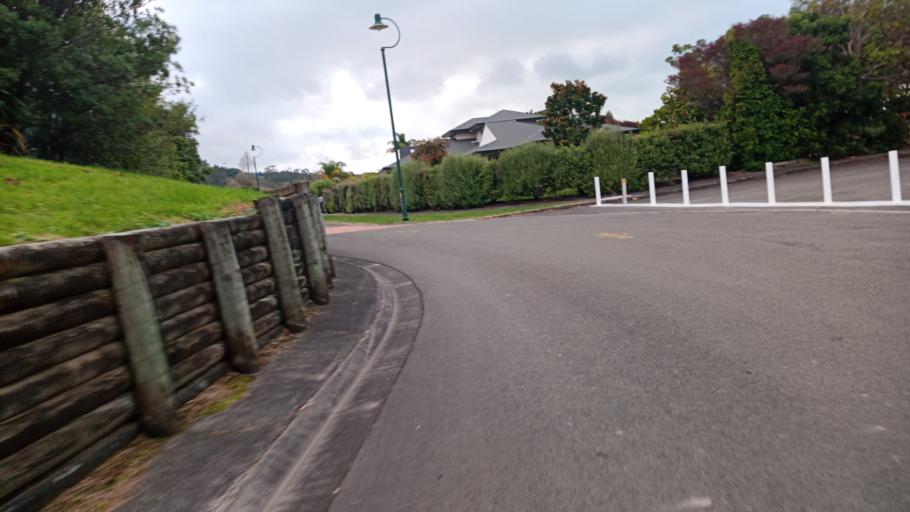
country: NZ
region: Gisborne
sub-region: Gisborne District
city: Gisborne
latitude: -38.6420
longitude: 178.0176
